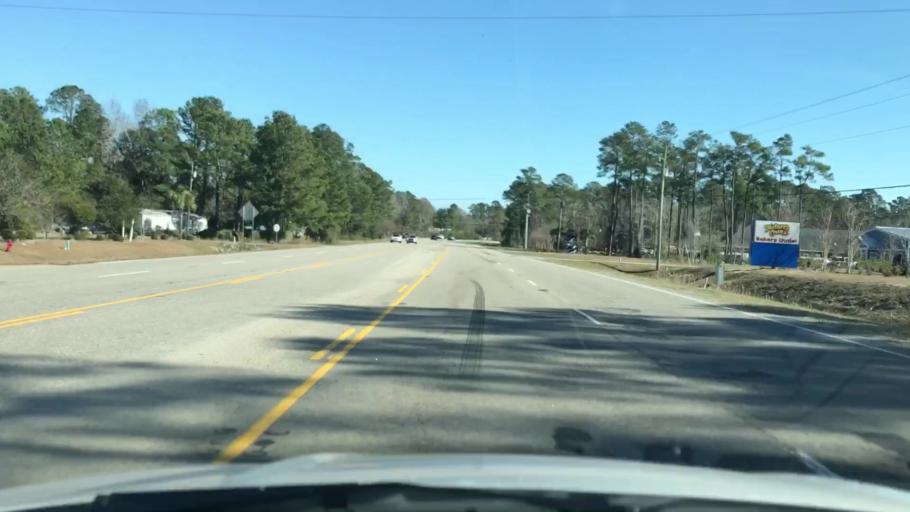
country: US
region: South Carolina
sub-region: Horry County
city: Garden City
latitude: 33.6301
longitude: -79.0239
